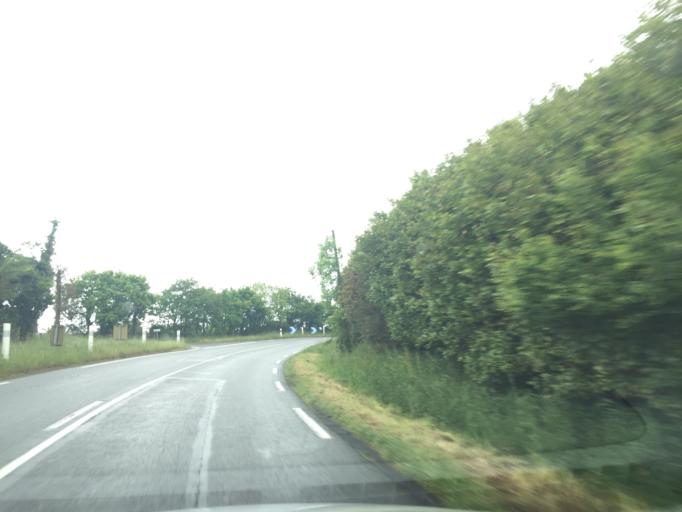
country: FR
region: Brittany
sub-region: Departement des Cotes-d'Armor
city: Ploubalay
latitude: 48.5880
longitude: -2.1187
